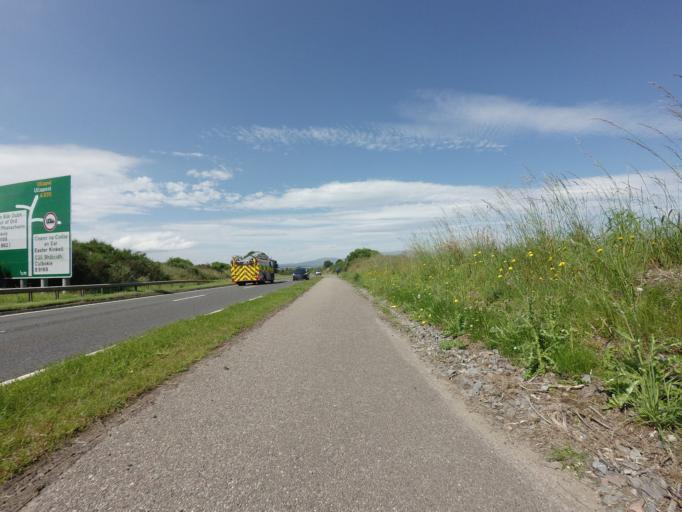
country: GB
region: Scotland
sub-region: Highland
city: Conon Bridge
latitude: 57.5486
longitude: -4.3921
